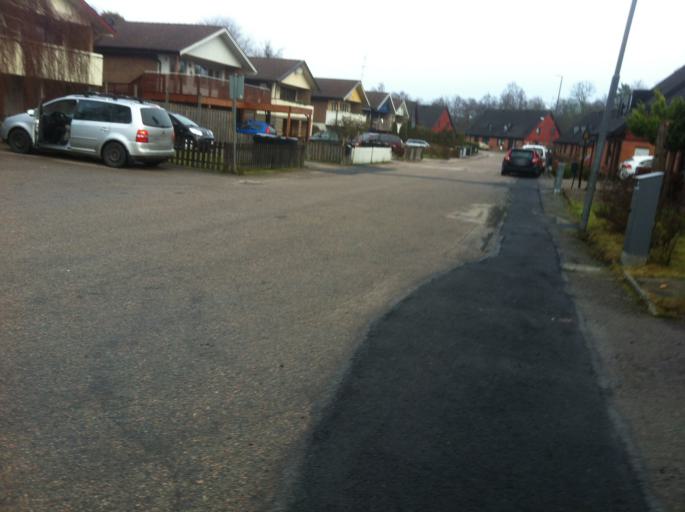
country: SE
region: Skane
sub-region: Perstorps Kommun
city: Perstorp
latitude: 56.1479
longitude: 13.3781
